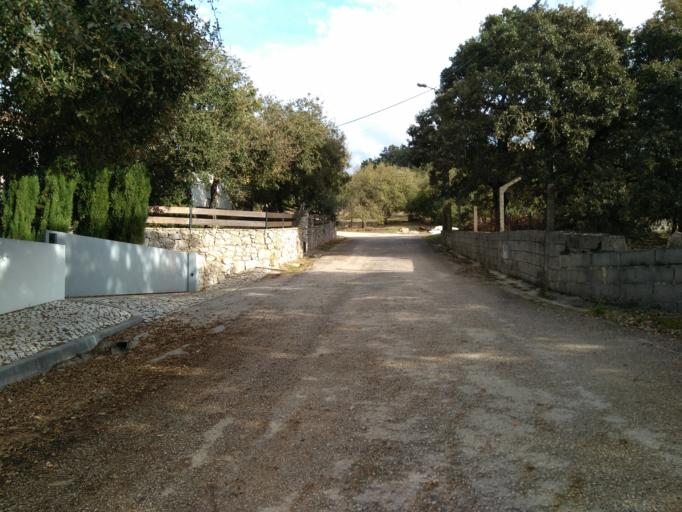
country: PT
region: Leiria
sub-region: Porto de Mos
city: Porto de Mos
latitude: 39.5953
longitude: -8.8063
